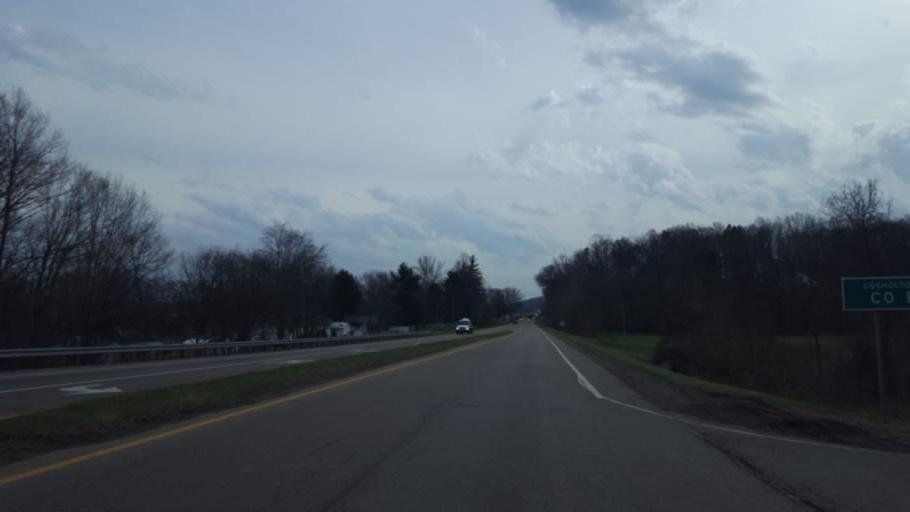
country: US
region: Ohio
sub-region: Coshocton County
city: Coshocton
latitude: 40.2479
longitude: -81.8734
